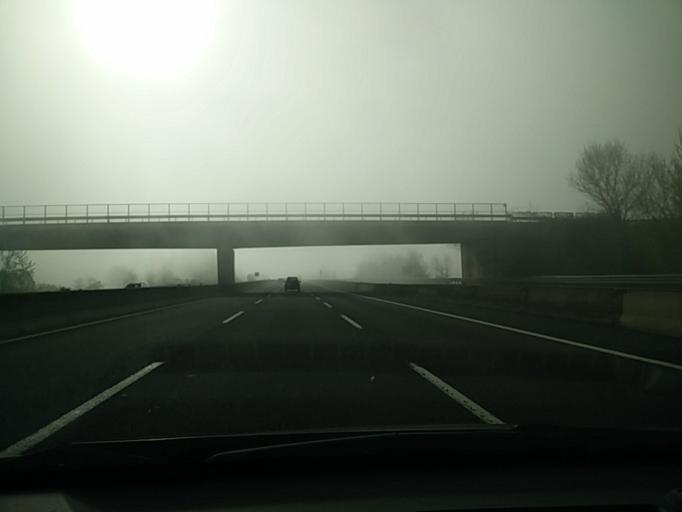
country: IT
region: Emilia-Romagna
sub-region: Provincia di Bologna
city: Ozzano dell'Emilia
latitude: 44.4713
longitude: 11.4728
